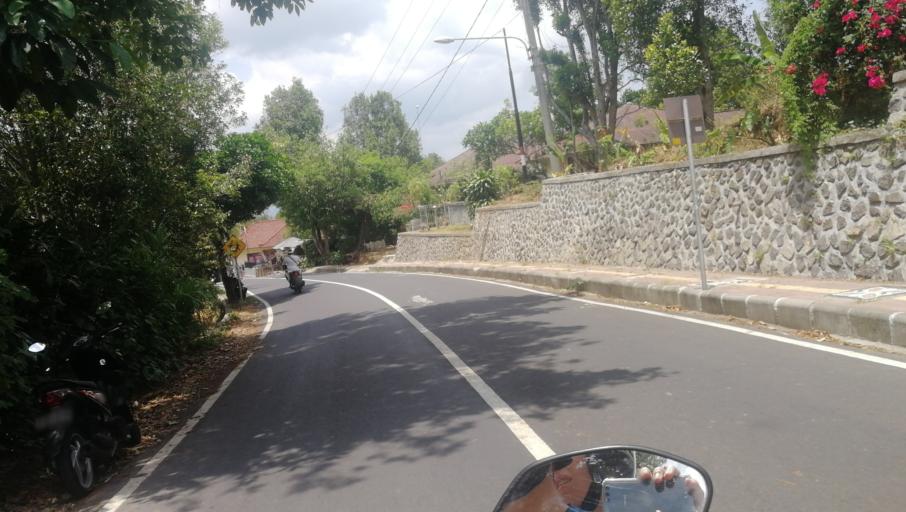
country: ID
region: Bali
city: Munduk
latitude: -8.2641
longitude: 115.0498
